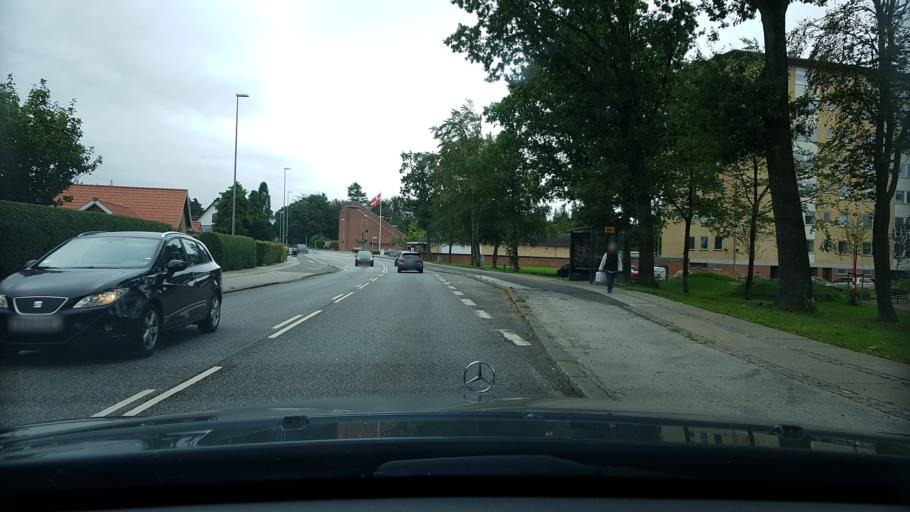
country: DK
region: Central Jutland
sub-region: Randers Kommune
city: Randers
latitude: 56.4784
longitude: 10.0408
